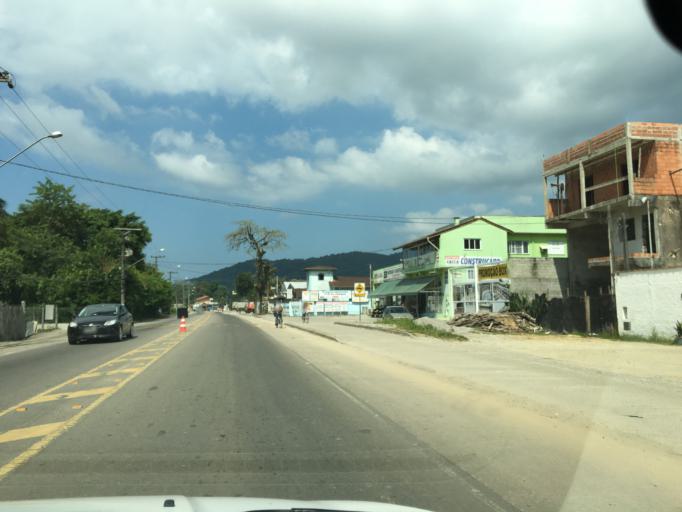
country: BR
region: Sao Paulo
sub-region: Ubatuba
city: Ubatuba
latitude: -23.4346
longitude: -45.1046
